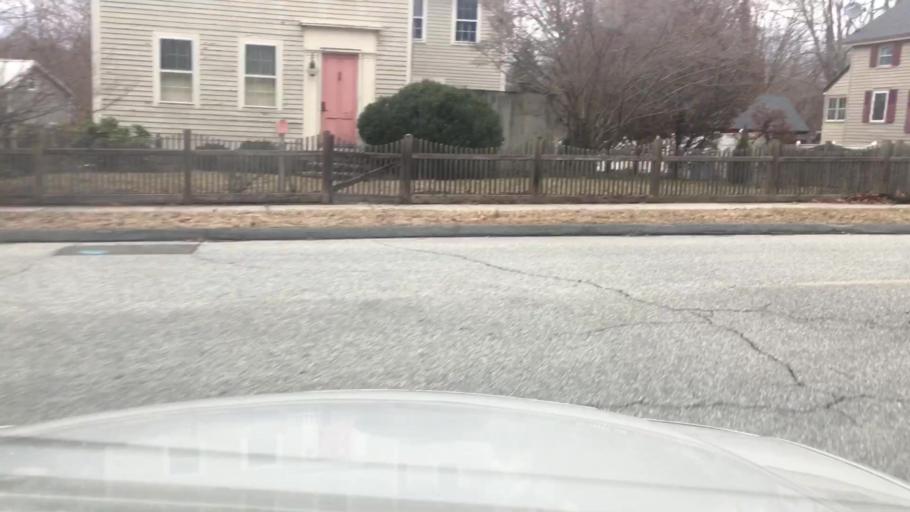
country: US
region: Connecticut
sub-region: Middlesex County
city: Essex Village
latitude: 41.3596
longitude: -72.3972
